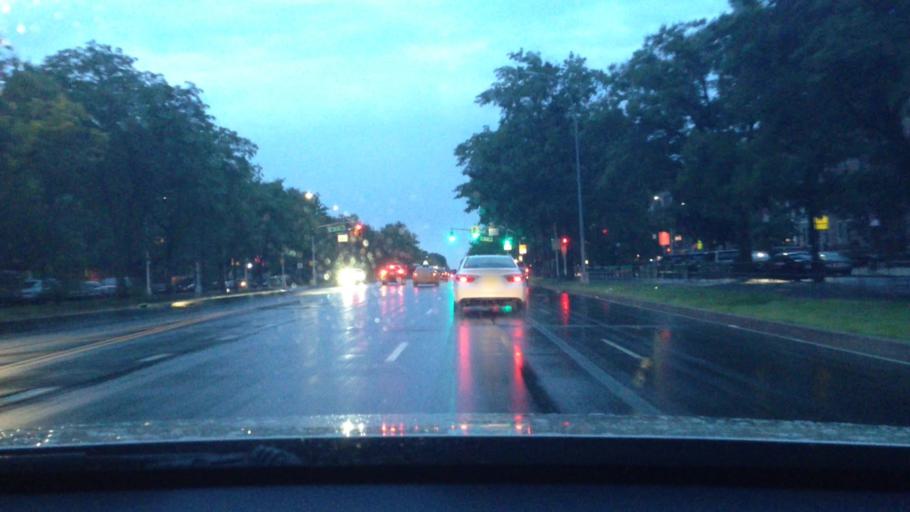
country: US
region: New York
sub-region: Kings County
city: Brooklyn
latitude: 40.6341
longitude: -73.9724
